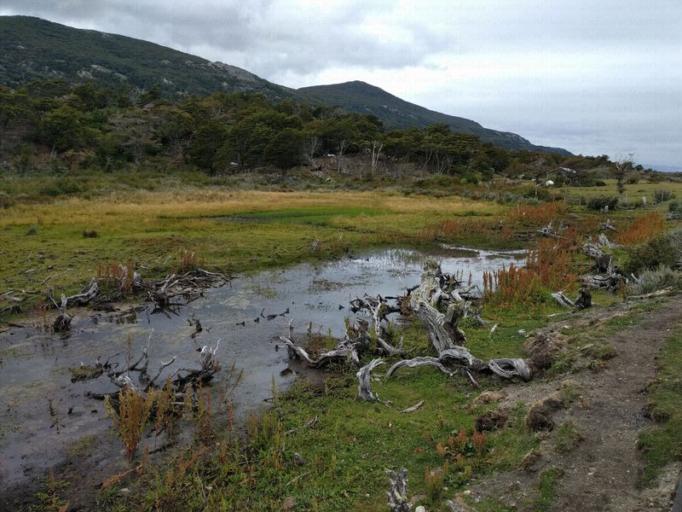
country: AR
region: Tierra del Fuego
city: Ushuaia
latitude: -54.8868
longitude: -67.6910
